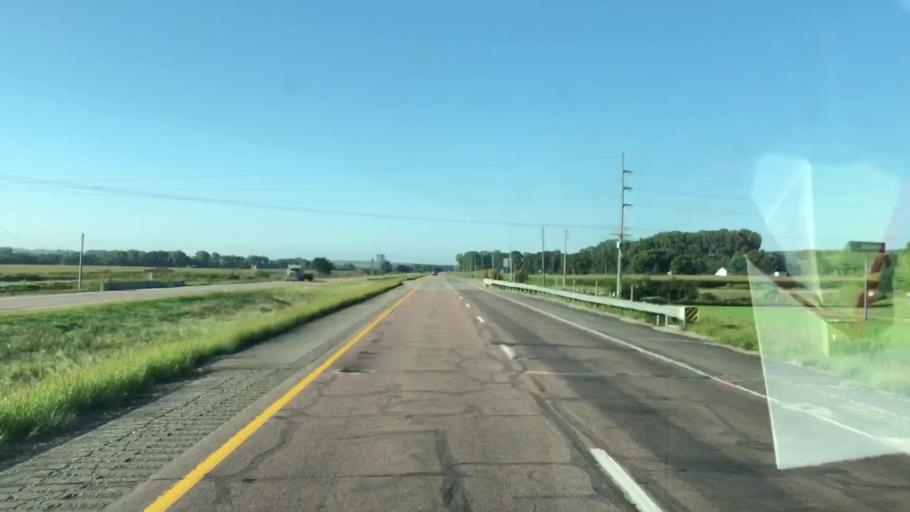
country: US
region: Iowa
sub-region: Woodbury County
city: Sioux City
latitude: 42.5949
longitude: -96.3048
